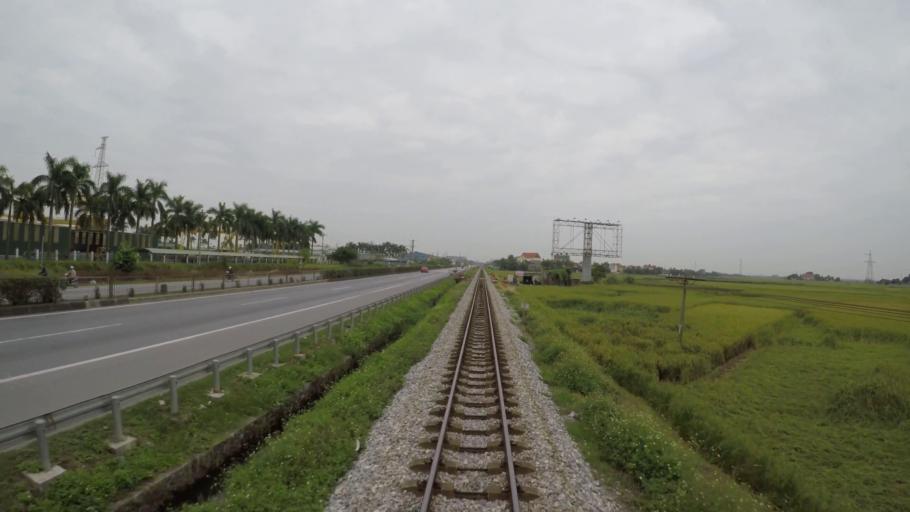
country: VN
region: Hai Duong
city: Phu Thai
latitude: 20.9484
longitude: 106.5356
